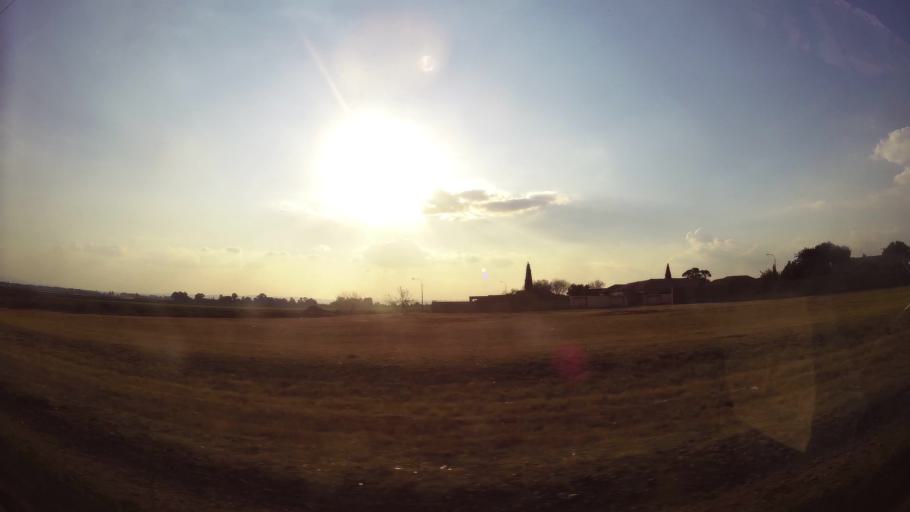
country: ZA
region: Gauteng
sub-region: Ekurhuleni Metropolitan Municipality
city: Boksburg
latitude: -26.3204
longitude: 28.2471
